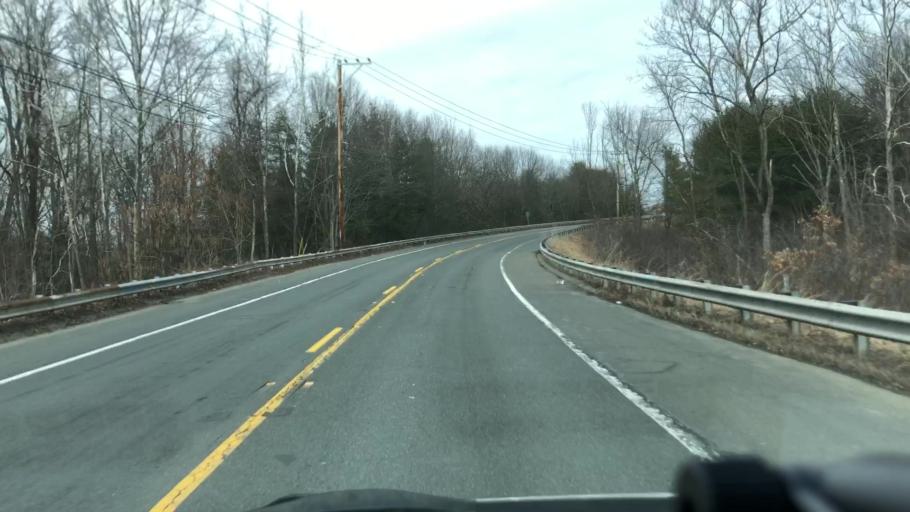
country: US
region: Massachusetts
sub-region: Hampshire County
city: Hatfield
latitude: 42.3968
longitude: -72.6304
